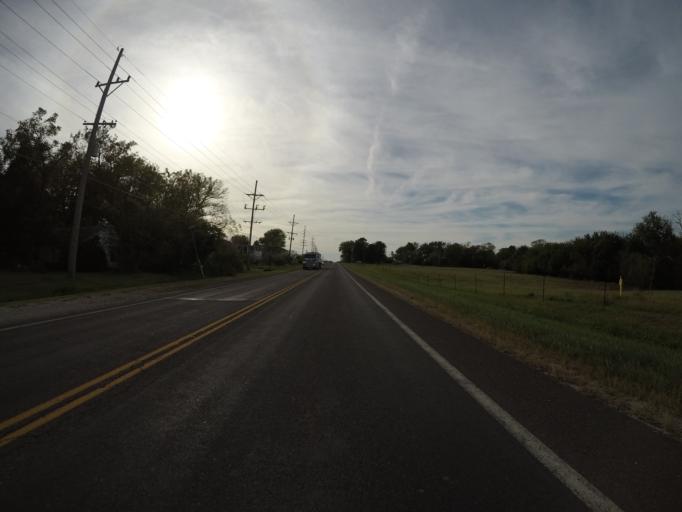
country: US
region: Kansas
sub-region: Johnson County
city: Edgerton
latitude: 38.7677
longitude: -95.0173
